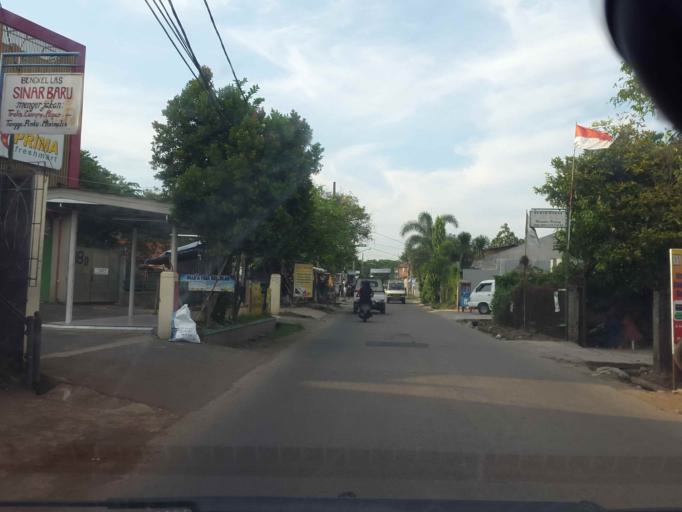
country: ID
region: West Java
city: Ciputat
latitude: -6.2550
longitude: 106.6886
